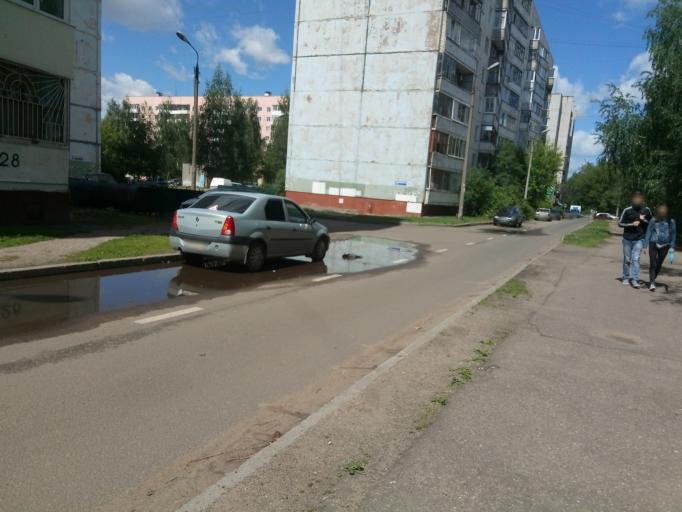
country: RU
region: Jaroslavl
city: Yaroslavl
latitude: 57.6510
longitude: 39.9635
